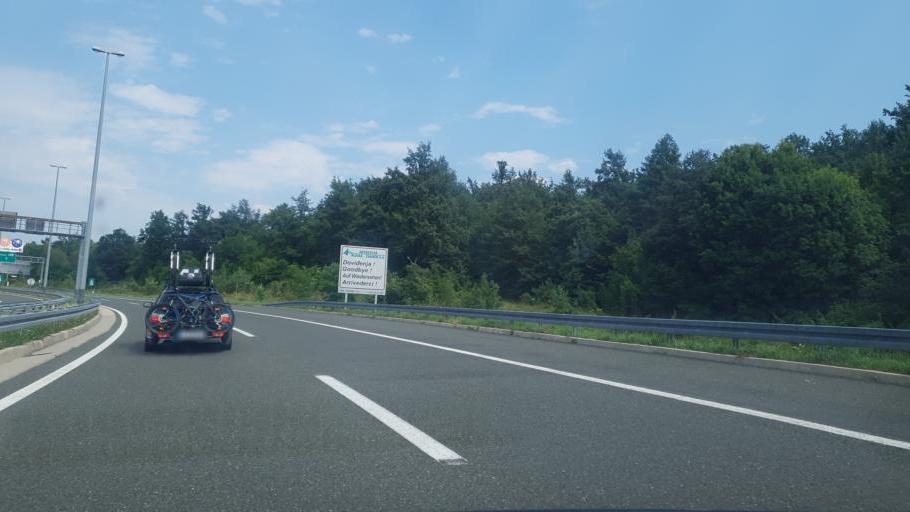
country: SI
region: Ilirska Bistrica
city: Ilirska Bistrica
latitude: 45.4851
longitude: 14.2816
